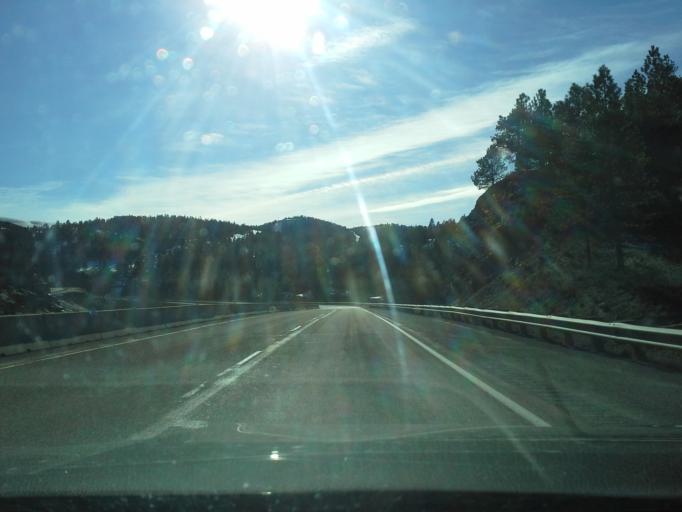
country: US
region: Montana
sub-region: Lewis and Clark County
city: Helena Valley Northwest
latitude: 46.9393
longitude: -112.1261
